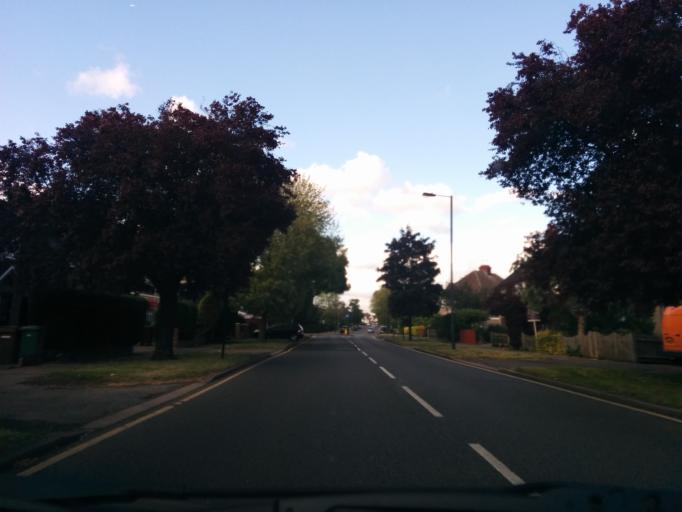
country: GB
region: England
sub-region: Greater London
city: Greenhill
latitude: 51.5759
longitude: -0.3480
